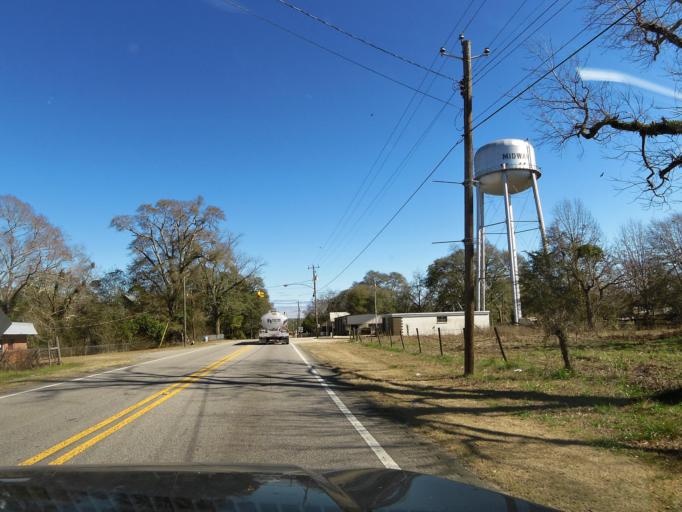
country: US
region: Alabama
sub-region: Bullock County
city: Union Springs
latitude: 32.0786
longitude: -85.5226
